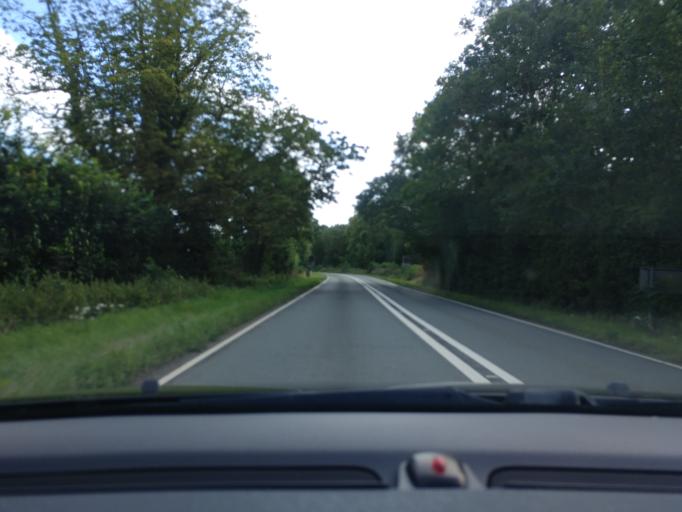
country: GB
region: England
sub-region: Oxfordshire
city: Bicester
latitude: 51.9047
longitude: -1.2242
